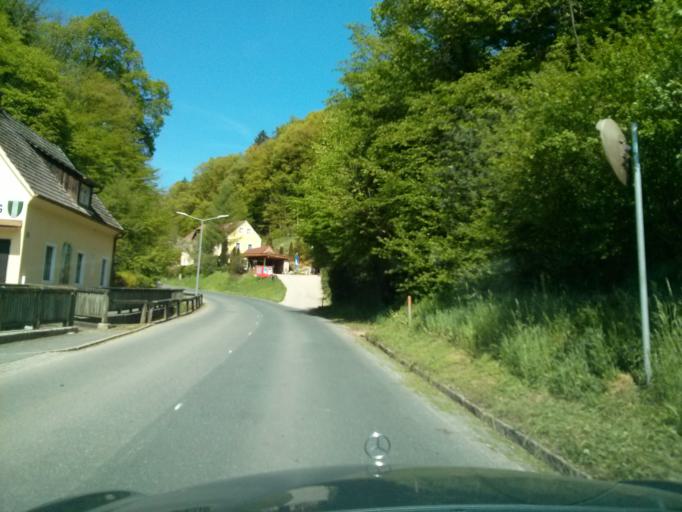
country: AT
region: Styria
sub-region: Politischer Bezirk Graz-Umgebung
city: Stattegg
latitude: 47.1439
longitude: 15.4191
